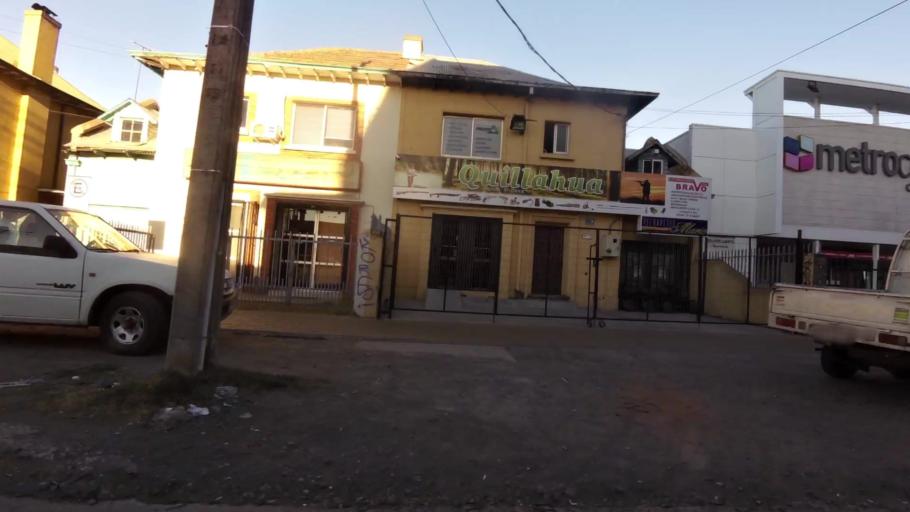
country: CL
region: Maule
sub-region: Provincia de Curico
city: Curico
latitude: -34.9804
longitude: -71.2407
